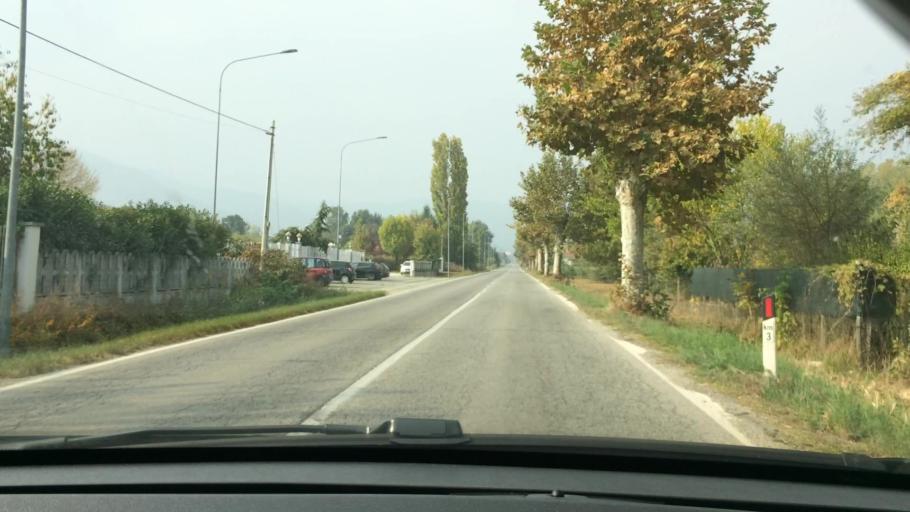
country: IT
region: Piedmont
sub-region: Provincia di Torino
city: Cumiana
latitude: 44.9613
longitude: 7.4016
